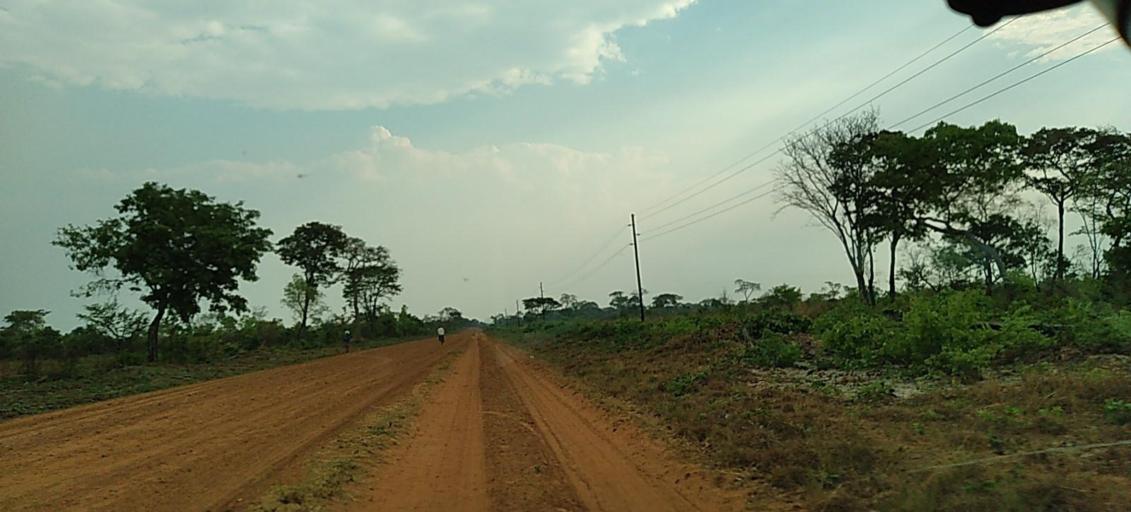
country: ZM
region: North-Western
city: Kabompo
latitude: -13.8908
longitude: 23.6597
